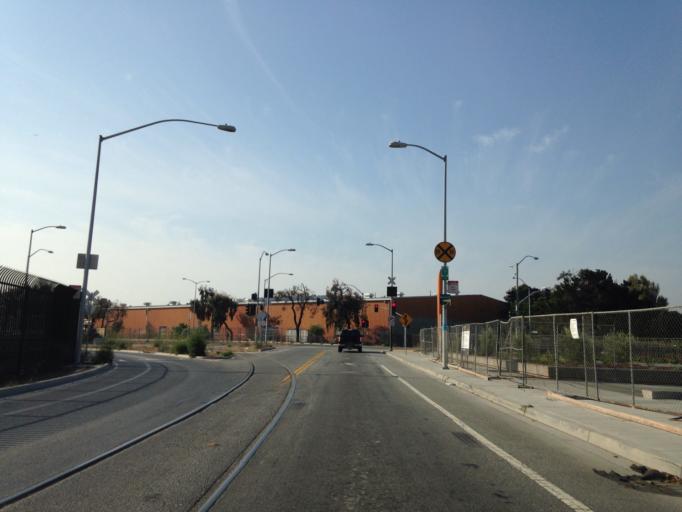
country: US
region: California
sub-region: San Francisco County
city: San Francisco
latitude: 37.7464
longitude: -122.3861
